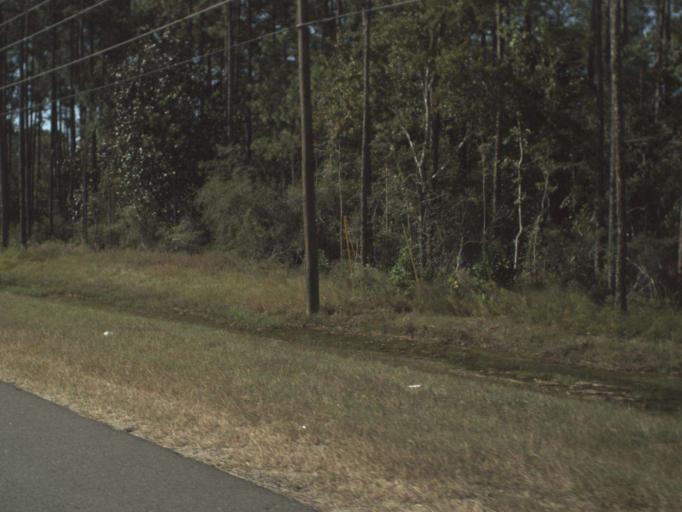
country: US
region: Florida
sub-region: Walton County
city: Freeport
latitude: 30.4618
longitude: -86.1312
